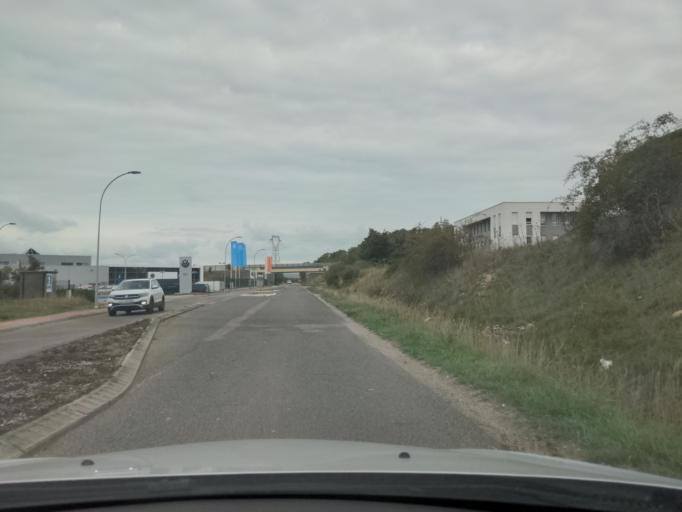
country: FR
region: Bourgogne
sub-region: Departement de la Cote-d'Or
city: Ahuy
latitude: 47.3570
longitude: 5.0400
